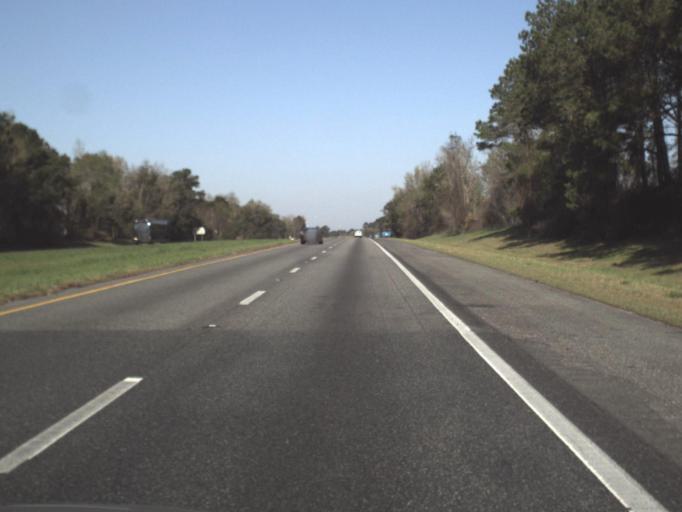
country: US
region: Florida
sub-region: Jefferson County
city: Monticello
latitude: 30.4491
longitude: -83.7484
